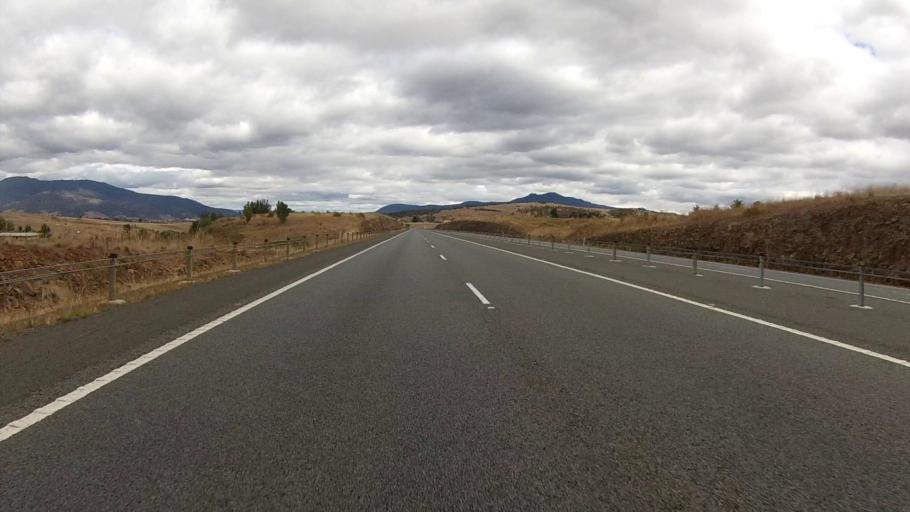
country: AU
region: Tasmania
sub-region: Brighton
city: Bridgewater
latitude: -42.7062
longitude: 147.2610
